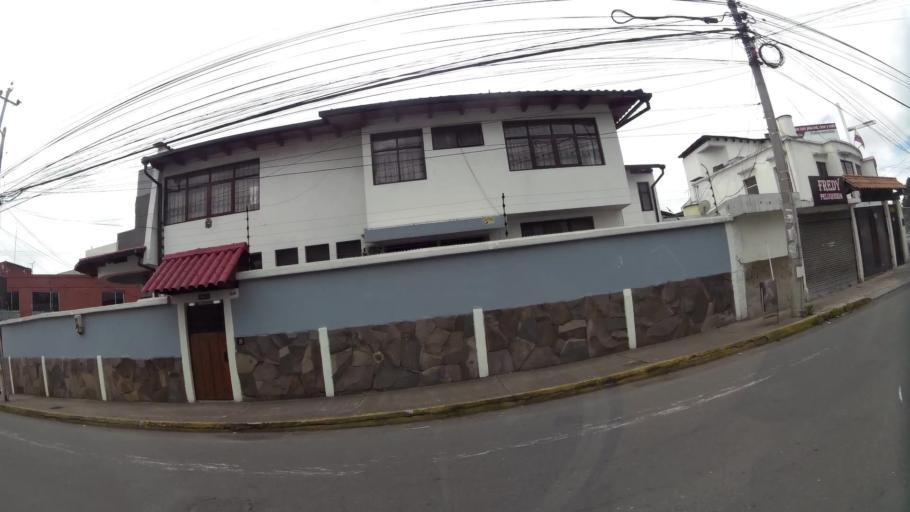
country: EC
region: Pichincha
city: Quito
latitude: -0.1595
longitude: -78.4902
